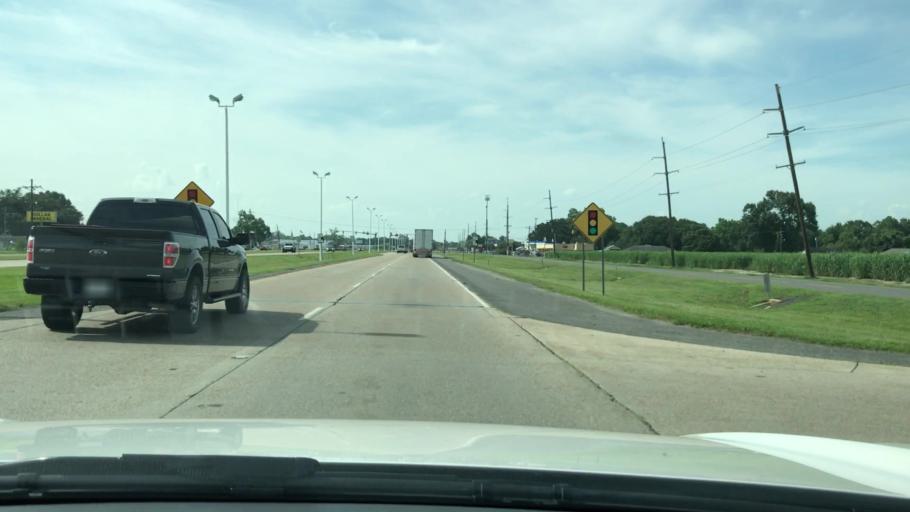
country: US
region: Louisiana
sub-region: West Baton Rouge Parish
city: Addis
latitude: 30.3532
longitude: -91.2586
